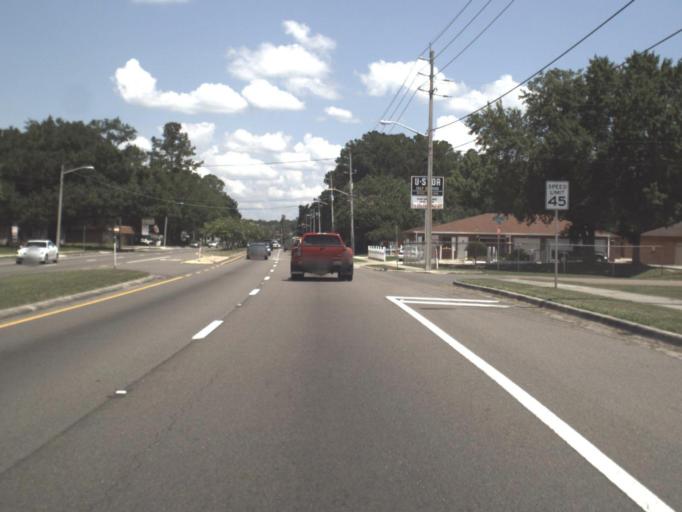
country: US
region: Florida
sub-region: Duval County
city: Jacksonville
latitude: 30.4309
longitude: -81.6942
